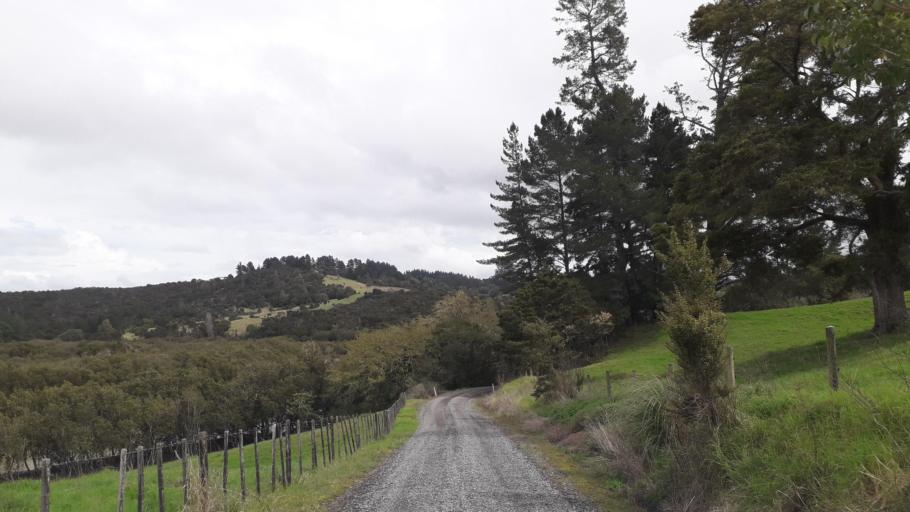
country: NZ
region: Northland
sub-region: Far North District
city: Waimate North
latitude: -35.3166
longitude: 173.5710
